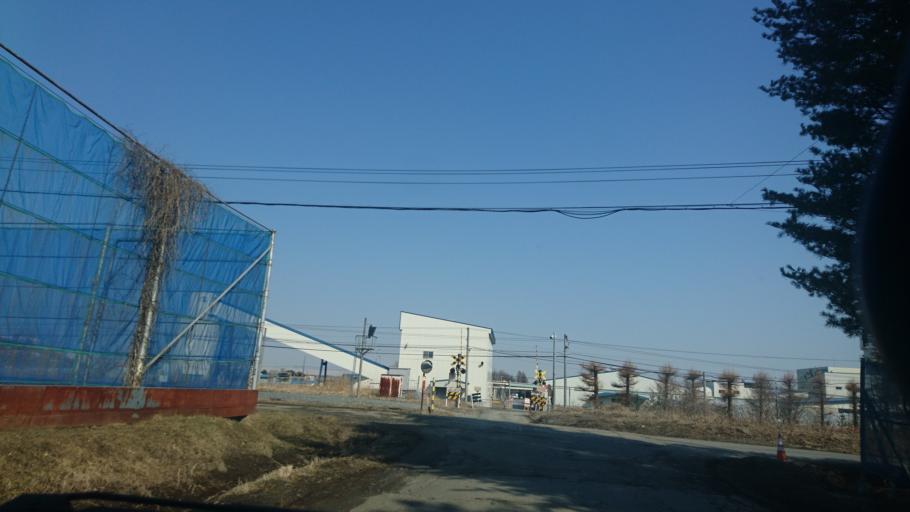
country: JP
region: Hokkaido
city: Obihiro
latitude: 42.9199
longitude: 143.0759
